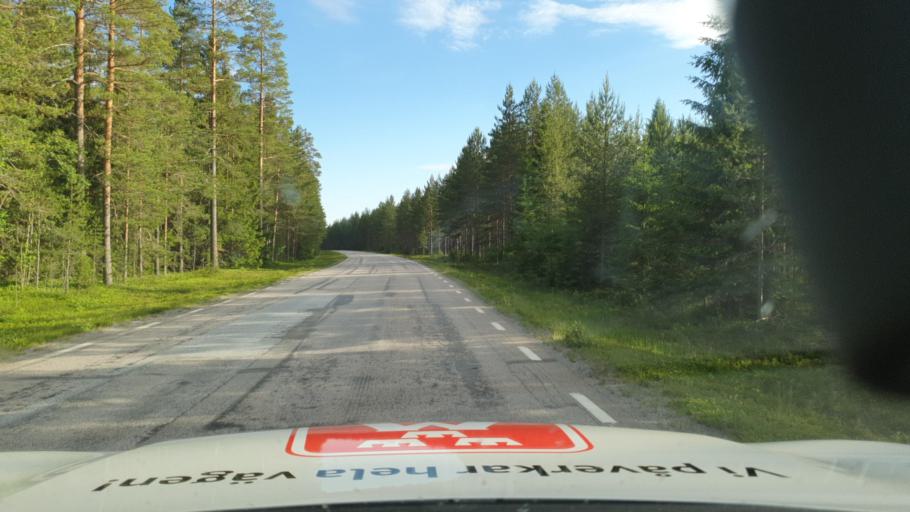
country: SE
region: Vaesterbotten
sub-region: Umea Kommun
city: Roback
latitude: 63.8685
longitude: 20.1468
